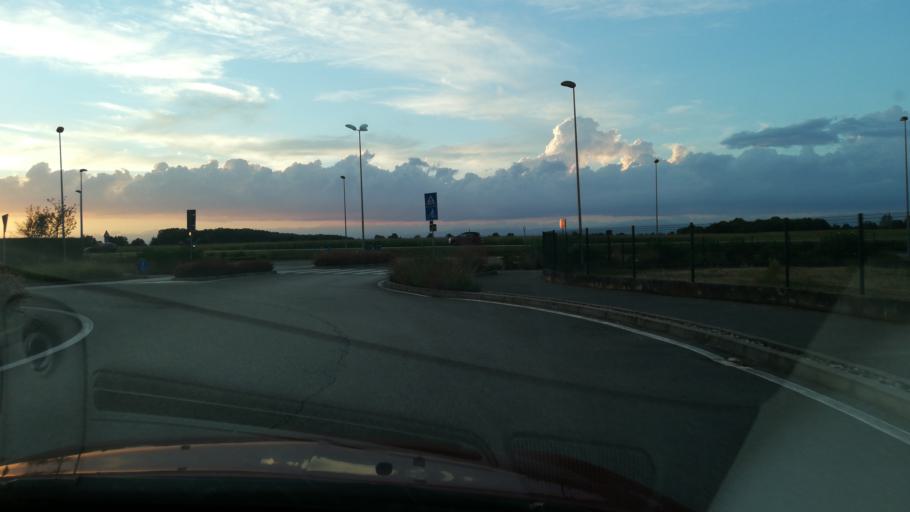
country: IT
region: Veneto
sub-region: Provincia di Venezia
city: Caorle
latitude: 45.5832
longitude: 12.8319
